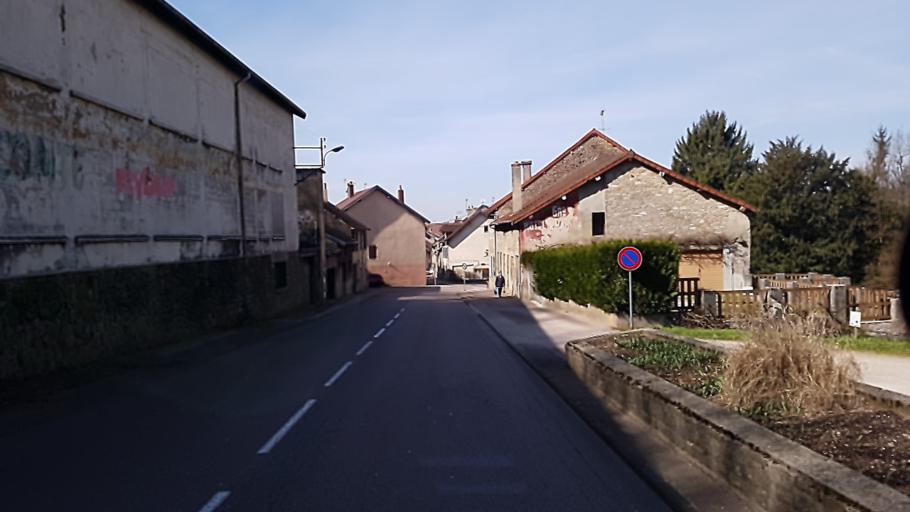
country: FR
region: Franche-Comte
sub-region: Departement du Jura
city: Poligny
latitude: 46.8328
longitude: 5.7126
